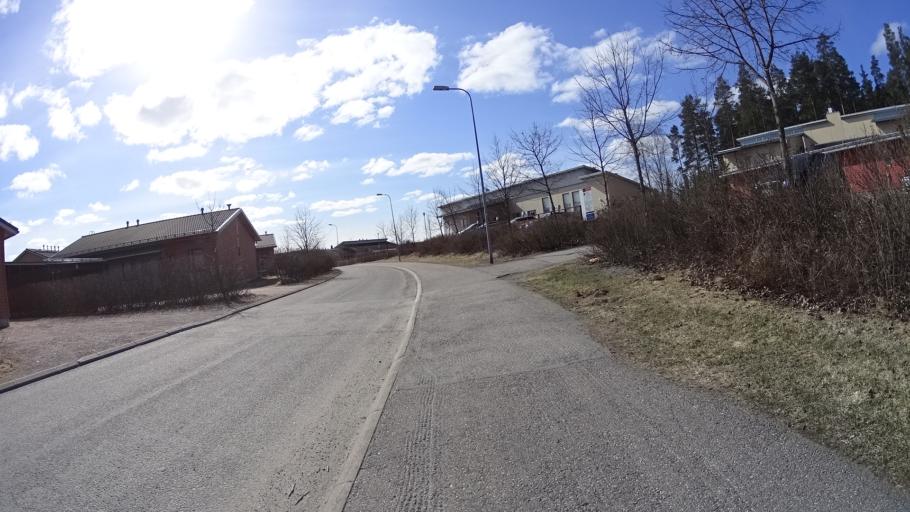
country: FI
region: Uusimaa
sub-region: Helsinki
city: Kauniainen
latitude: 60.2509
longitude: 24.7215
